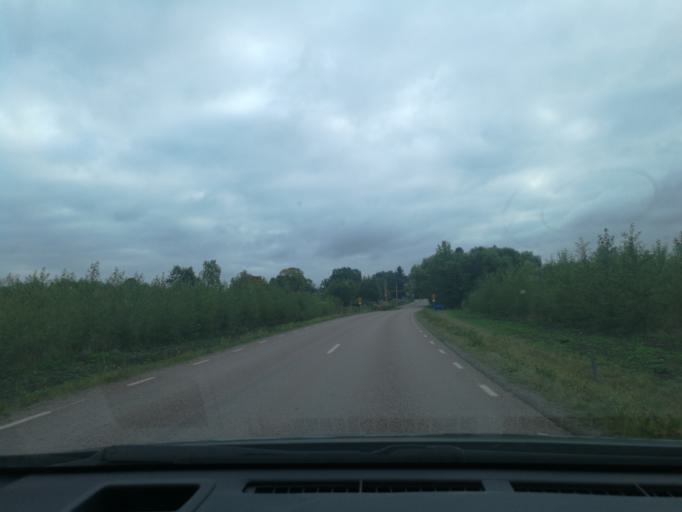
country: SE
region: Vaestmanland
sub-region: Vasteras
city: Tillberga
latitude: 59.6901
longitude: 16.6194
